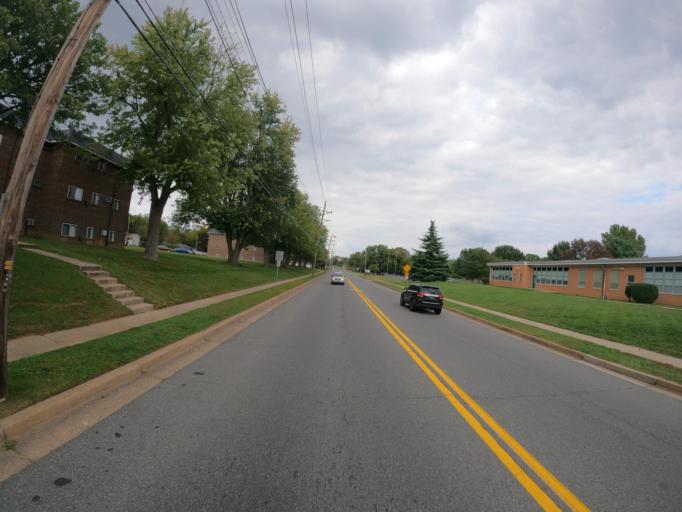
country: US
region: Delaware
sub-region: New Castle County
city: Brookside
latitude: 39.6679
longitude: -75.7273
